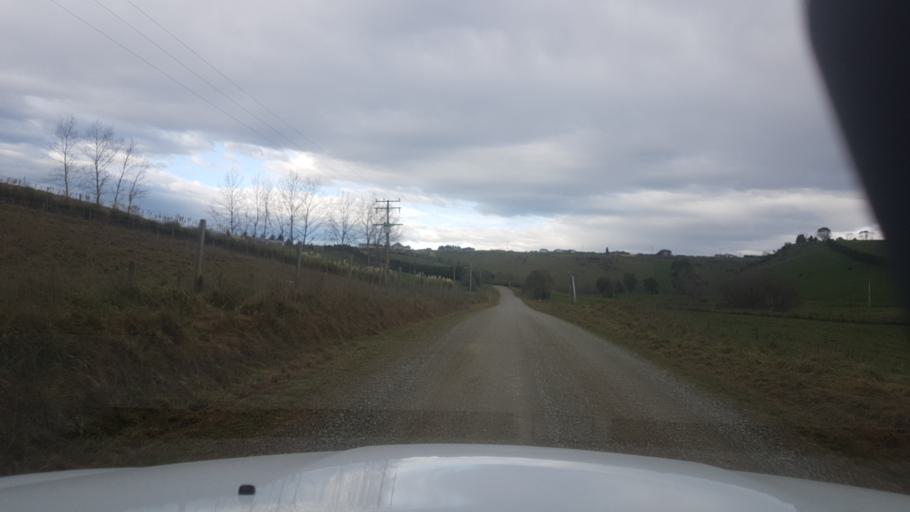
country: NZ
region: Canterbury
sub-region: Timaru District
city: Pleasant Point
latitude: -44.3460
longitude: 171.1580
